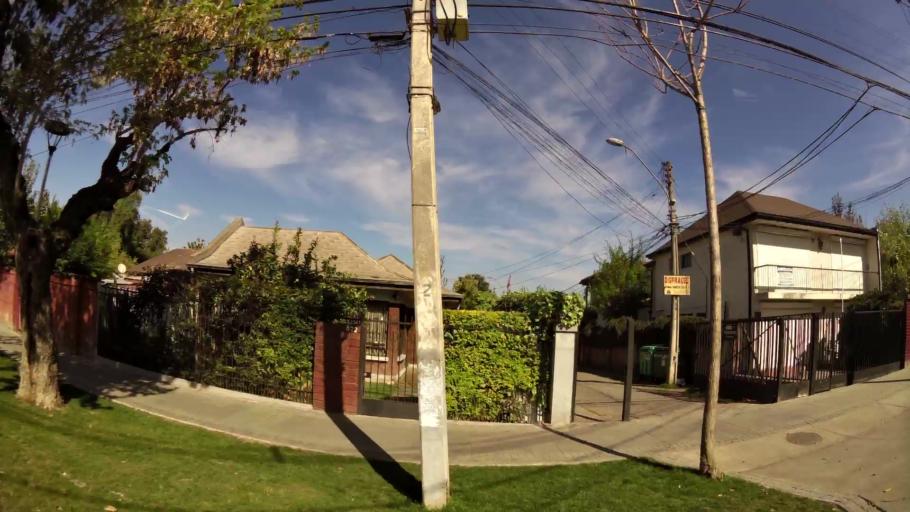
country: CL
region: Santiago Metropolitan
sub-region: Provincia de Santiago
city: Villa Presidente Frei, Nunoa, Santiago, Chile
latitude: -33.4454
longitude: -70.5665
